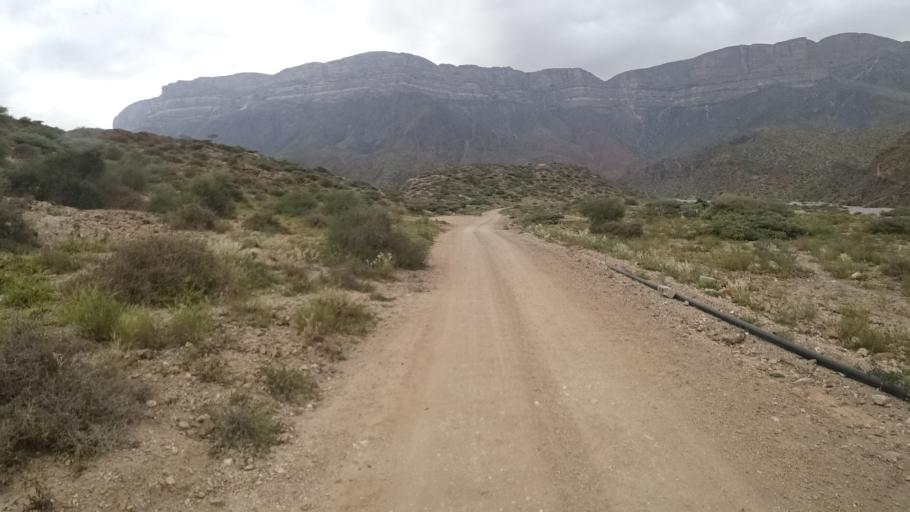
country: OM
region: Zufar
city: Salalah
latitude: 17.1717
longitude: 54.9524
